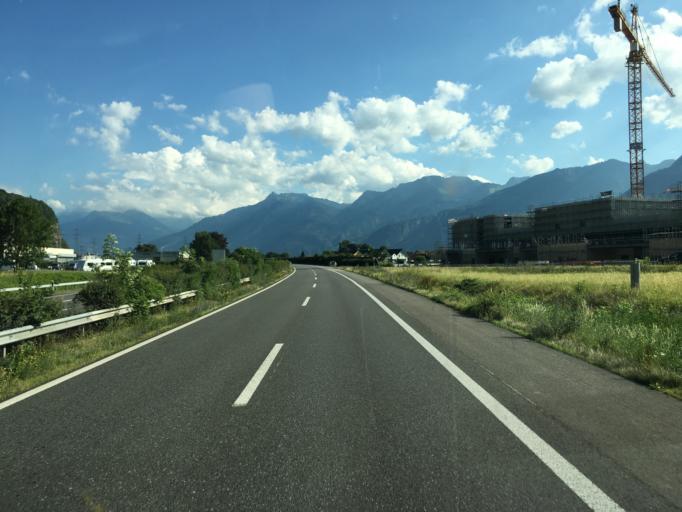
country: CH
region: Vaud
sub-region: Aigle District
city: Villeneuve
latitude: 46.3809
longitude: 6.9234
